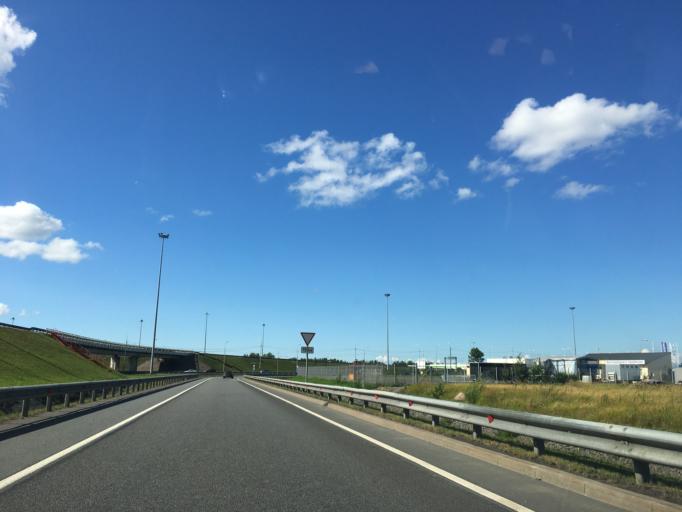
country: RU
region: St.-Petersburg
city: Sosnovaya Polyana
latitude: 59.8008
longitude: 30.1622
